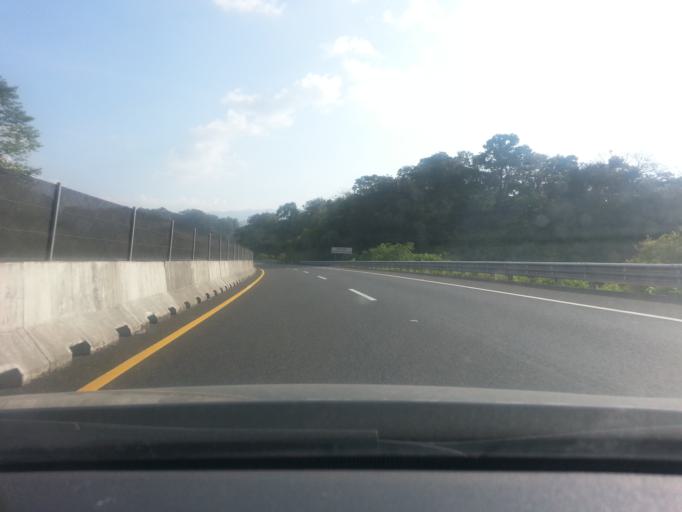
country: MX
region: Puebla
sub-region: Xicotepec
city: San Lorenzo
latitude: 20.4244
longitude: -97.9287
